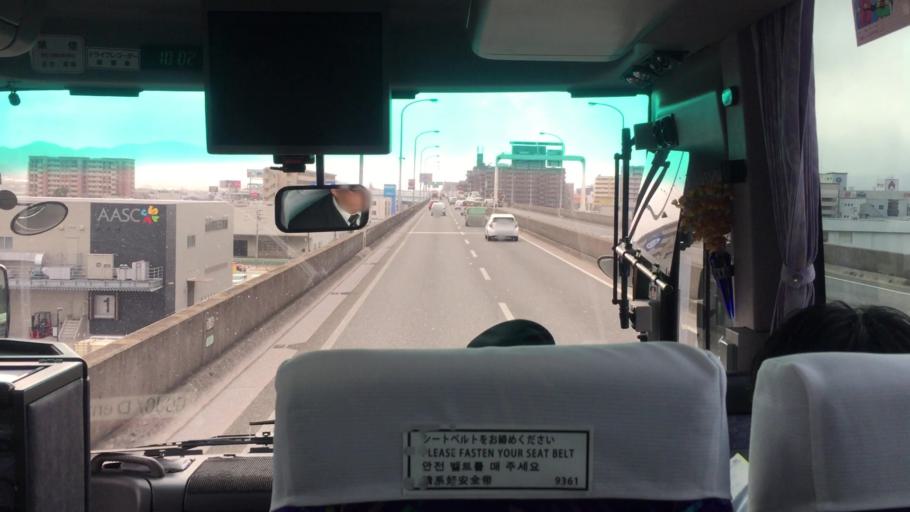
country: JP
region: Fukuoka
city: Fukuoka-shi
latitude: 33.5807
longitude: 130.4436
